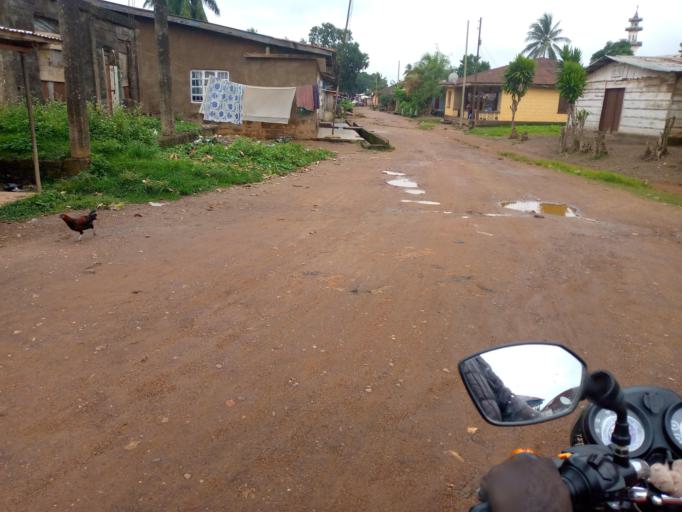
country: SL
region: Eastern Province
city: Kenema
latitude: 7.8860
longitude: -11.1864
